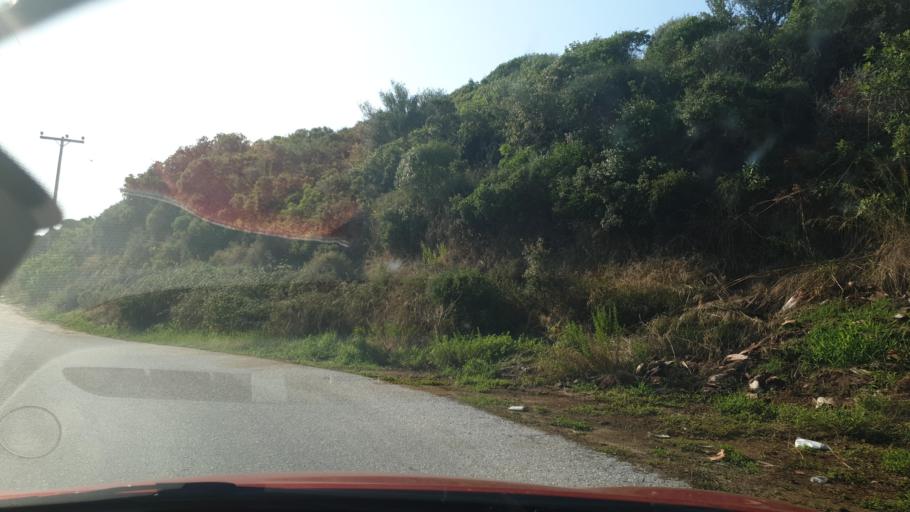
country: GR
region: Central Macedonia
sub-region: Nomos Chalkidikis
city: Sarti
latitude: 40.0824
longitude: 23.9783
